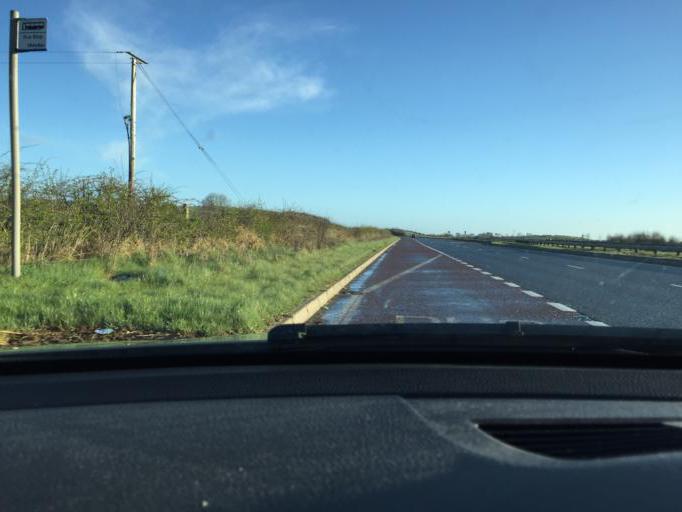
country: GB
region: Northern Ireland
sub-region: Banbridge District
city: Banbridge
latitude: 54.2980
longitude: -6.2981
